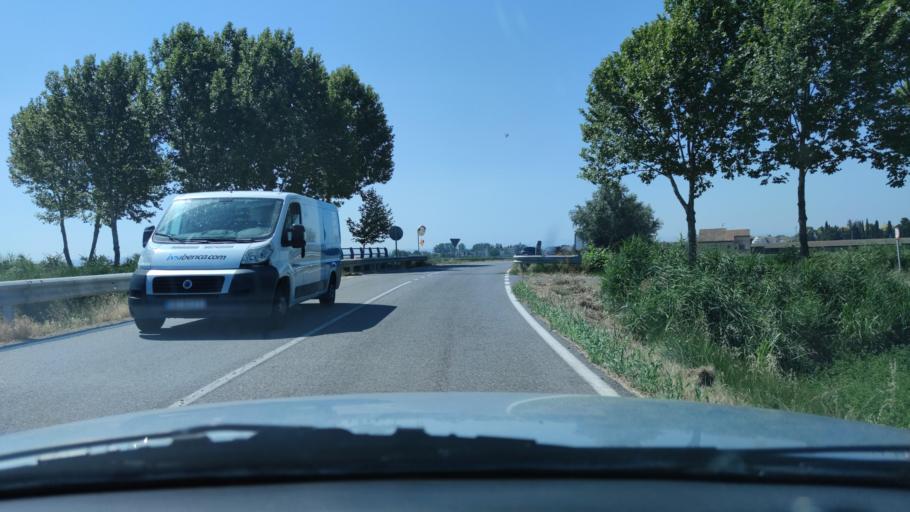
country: ES
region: Catalonia
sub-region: Provincia de Lleida
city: Ivars d'Urgell
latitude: 41.6913
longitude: 0.9900
